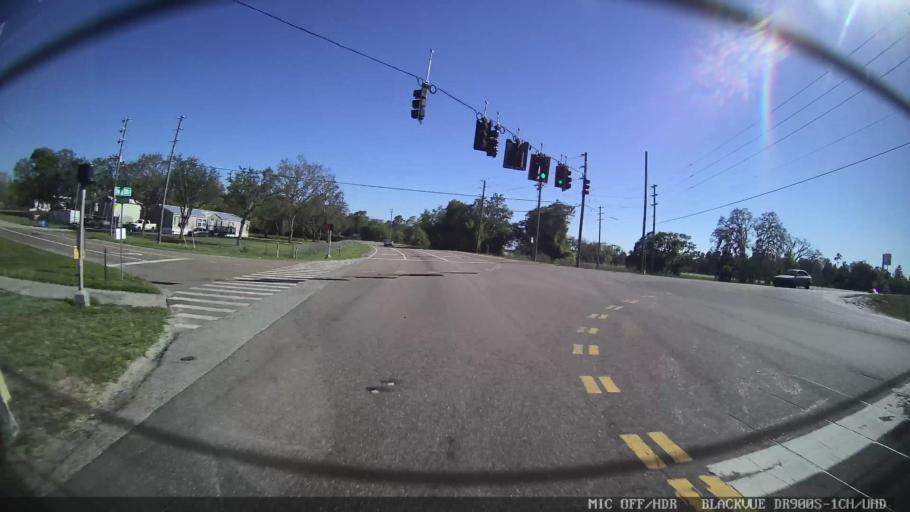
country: US
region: Florida
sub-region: Pasco County
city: Shady Hills
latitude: 28.3757
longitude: -82.5513
